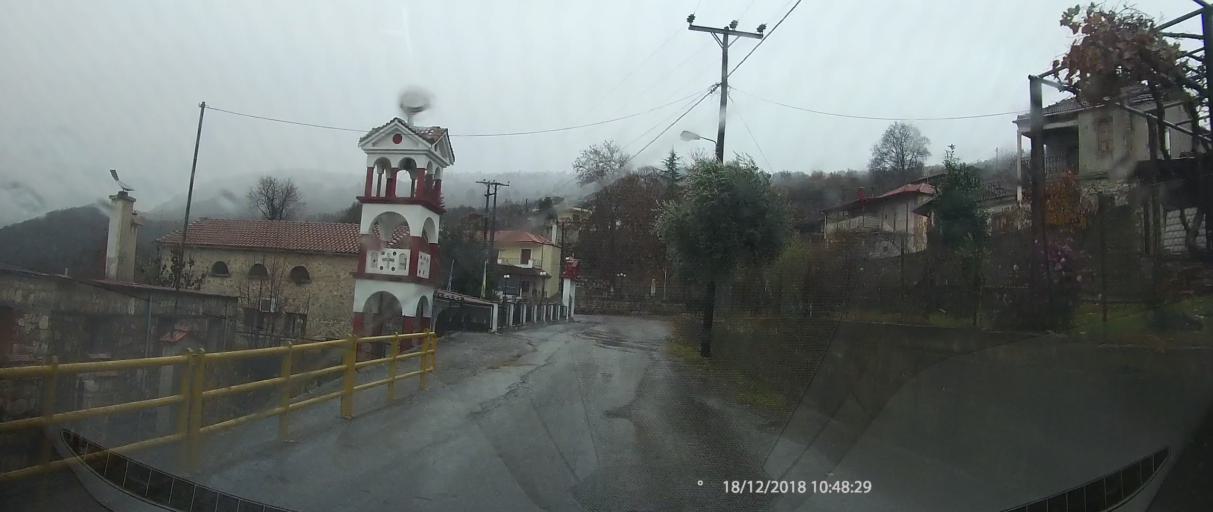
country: GR
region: Central Macedonia
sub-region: Nomos Pierias
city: Kato Milia
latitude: 40.1808
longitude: 22.3305
